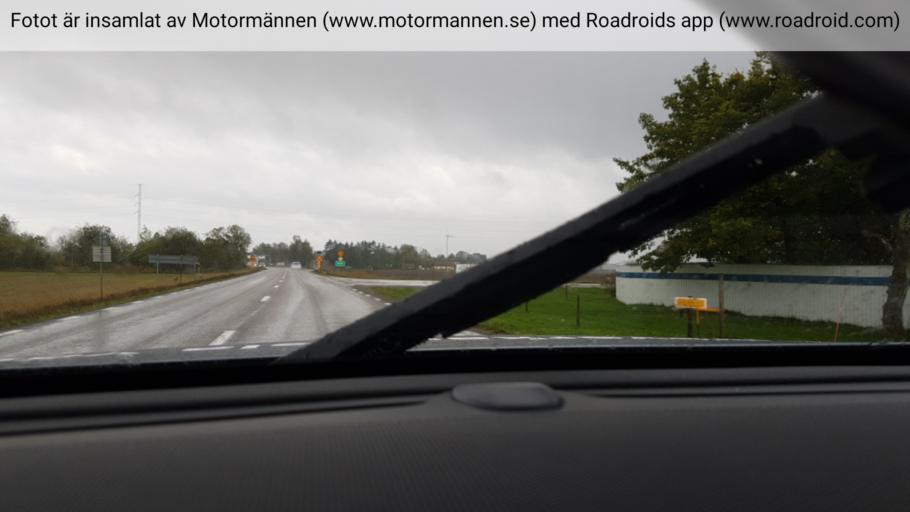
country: SE
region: Vaestra Goetaland
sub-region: Melleruds Kommun
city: Mellerud
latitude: 58.6384
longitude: 12.4120
